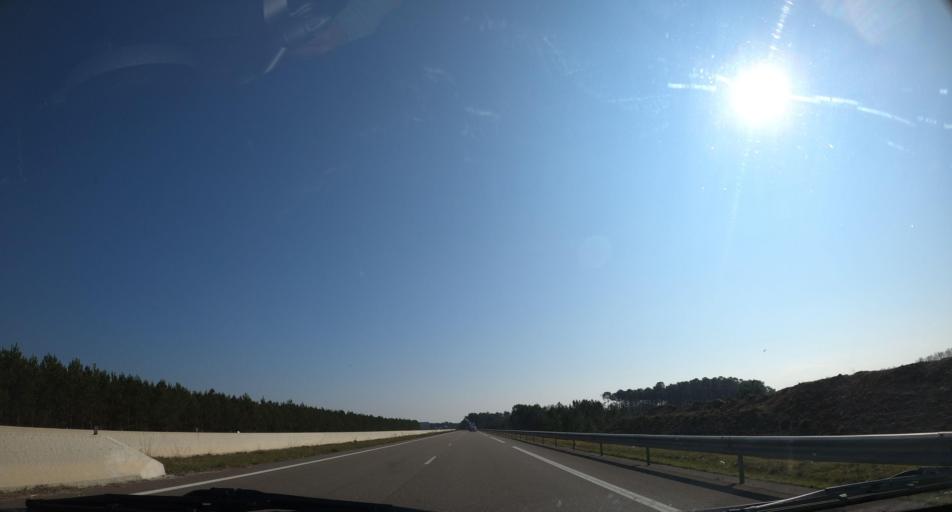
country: FR
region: Aquitaine
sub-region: Departement des Landes
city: Saint-Geours-de-Maremne
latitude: 43.6955
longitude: -1.2178
